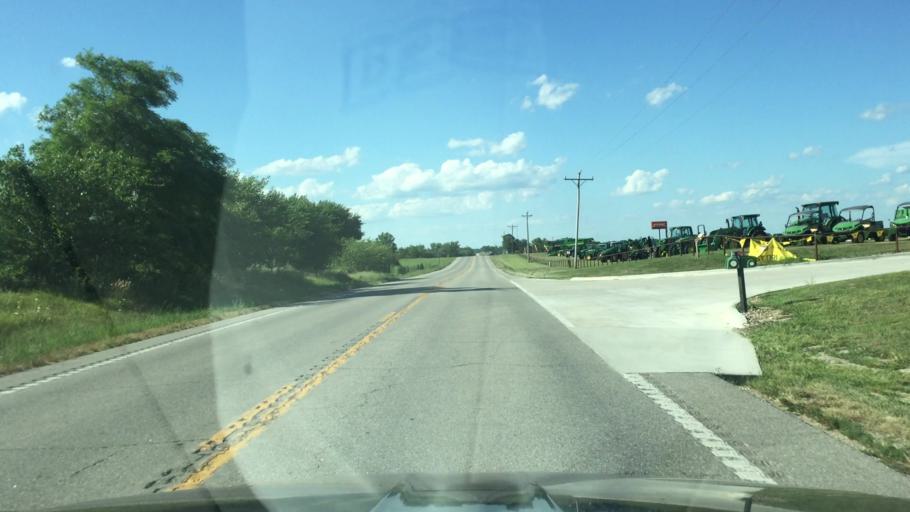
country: US
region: Missouri
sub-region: Moniteau County
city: Tipton
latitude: 38.6201
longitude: -92.7898
